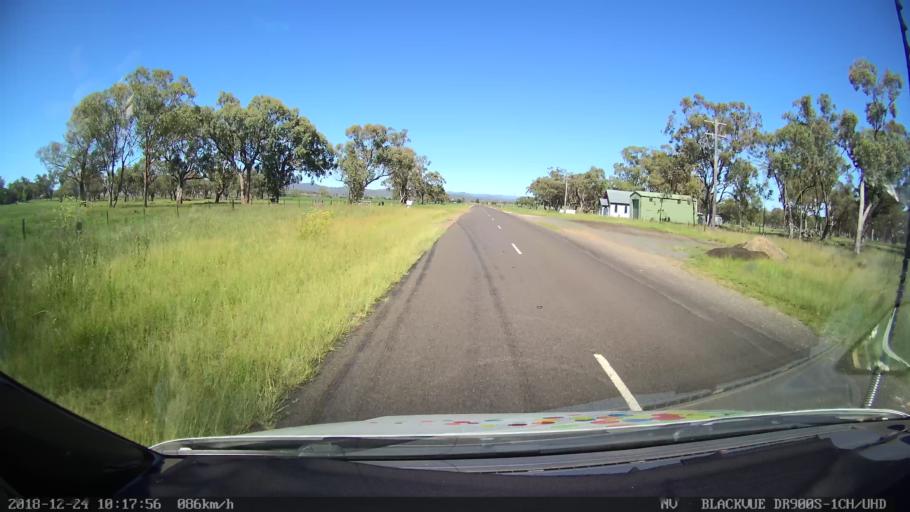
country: AU
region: New South Wales
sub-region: Liverpool Plains
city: Quirindi
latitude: -31.7219
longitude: 150.5838
